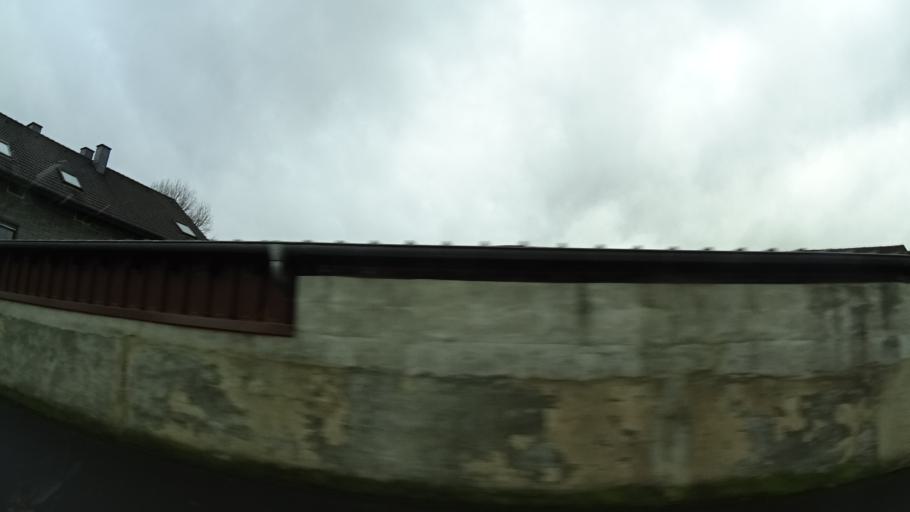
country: DE
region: Hesse
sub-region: Regierungsbezirk Darmstadt
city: Bad Soden-Salmunster
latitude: 50.2919
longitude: 9.3939
